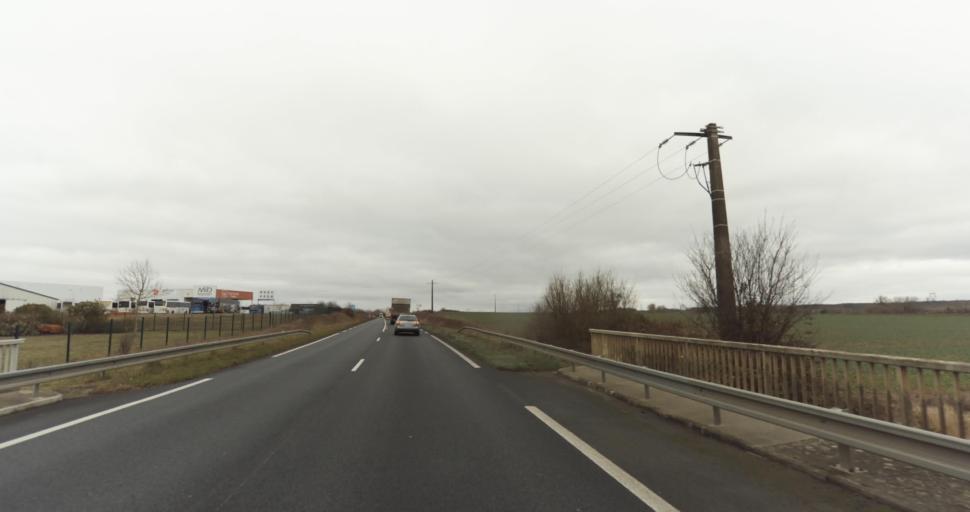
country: FR
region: Pays de la Loire
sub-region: Departement de Maine-et-Loire
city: Doue-la-Fontaine
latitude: 47.1898
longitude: -0.2433
